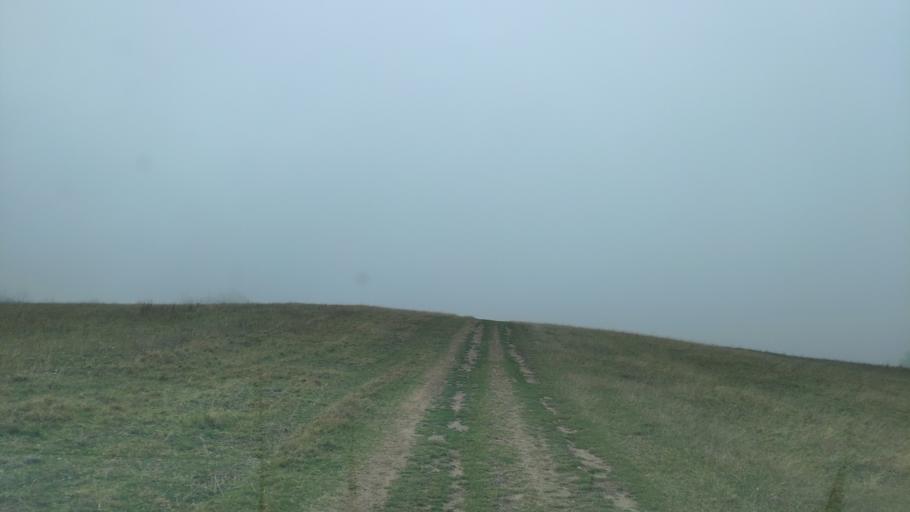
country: SK
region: Presovsky
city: Sabinov
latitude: 49.1492
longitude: 21.2366
